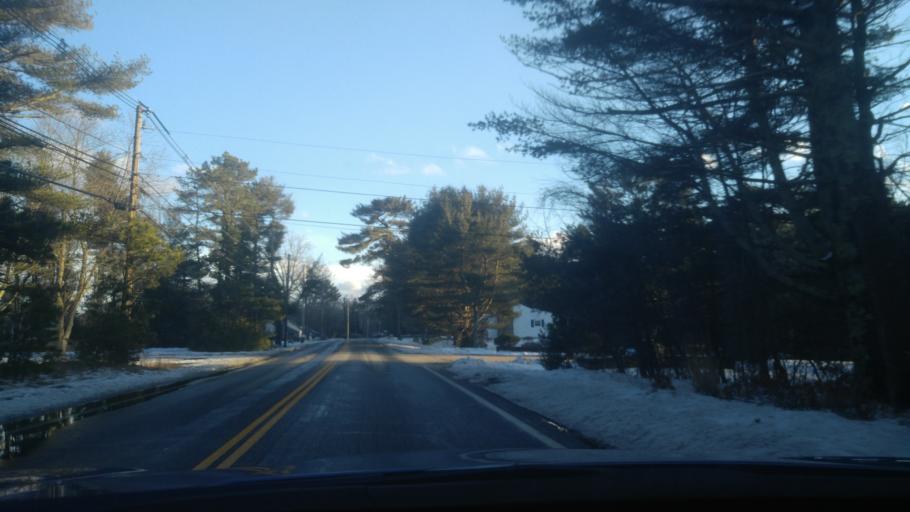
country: US
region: Rhode Island
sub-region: Kent County
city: West Greenwich
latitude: 41.6786
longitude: -71.6134
